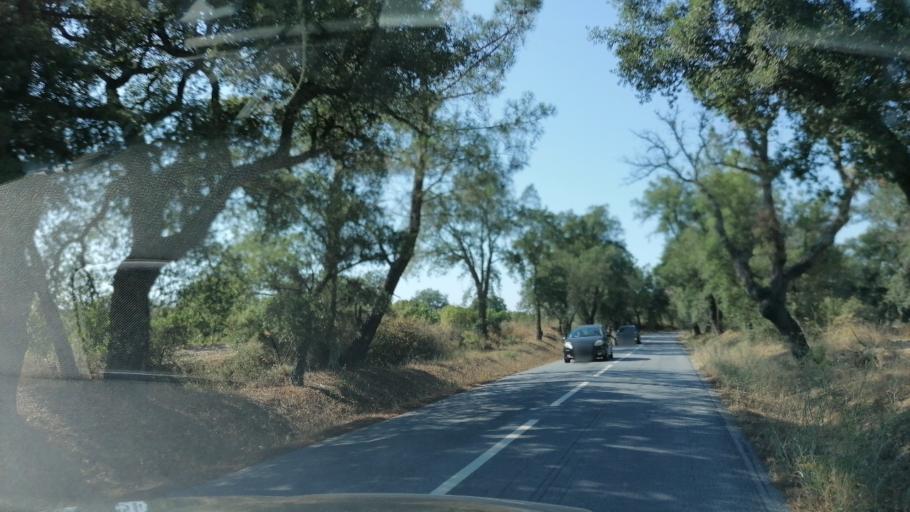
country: PT
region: Santarem
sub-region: Benavente
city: Poceirao
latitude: 38.7476
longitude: -8.6312
